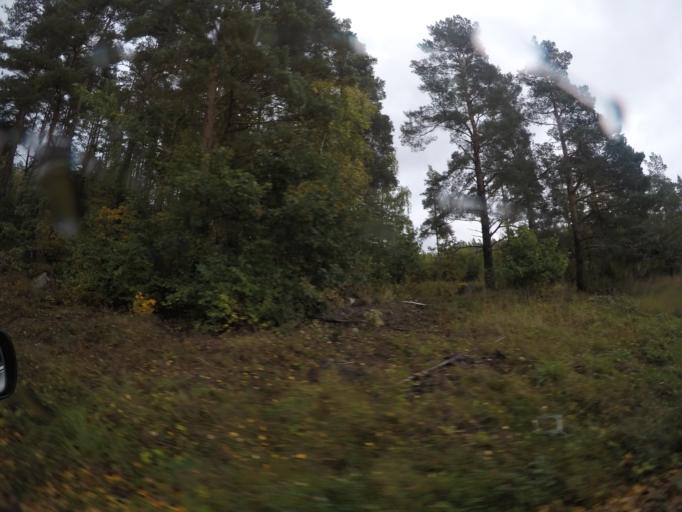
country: SE
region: Soedermanland
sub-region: Eskilstuna Kommun
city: Kvicksund
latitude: 59.3326
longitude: 16.2961
